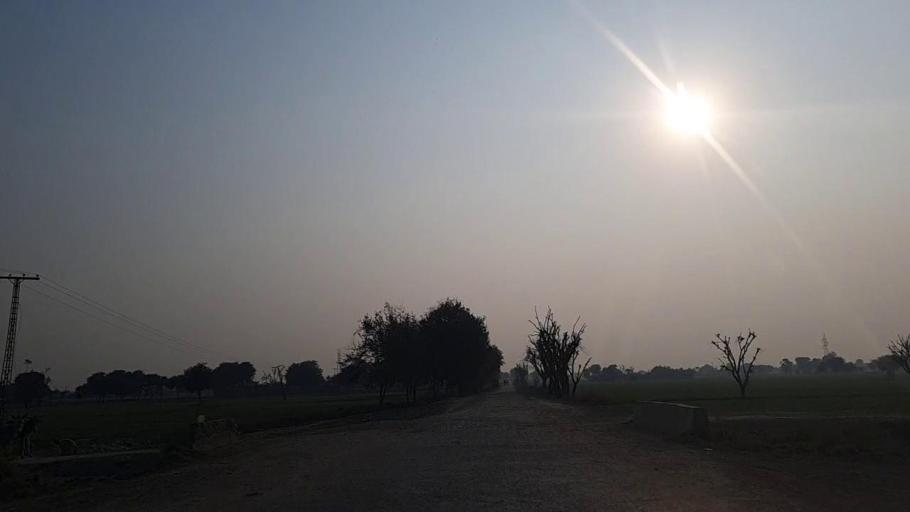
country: PK
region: Sindh
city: Nawabshah
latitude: 26.2294
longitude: 68.4839
